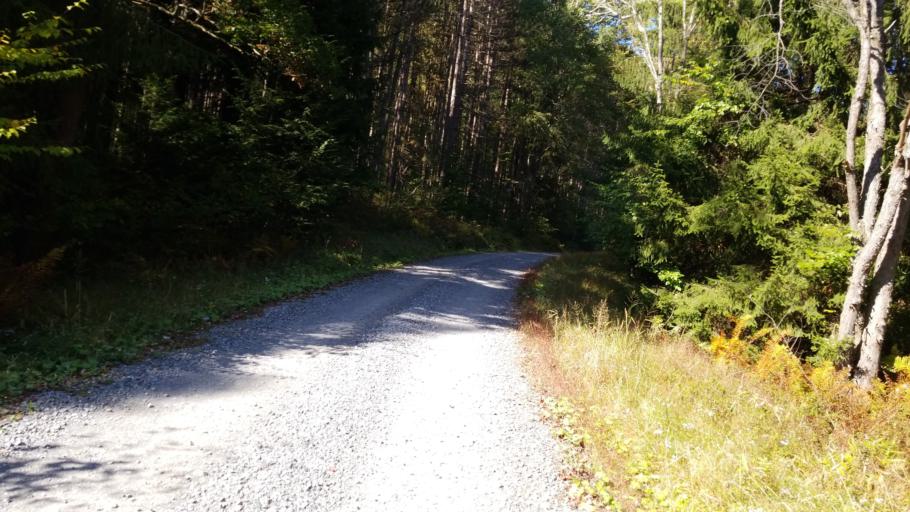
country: US
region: Pennsylvania
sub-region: Clearfield County
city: Clearfield
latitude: 41.1869
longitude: -78.5145
